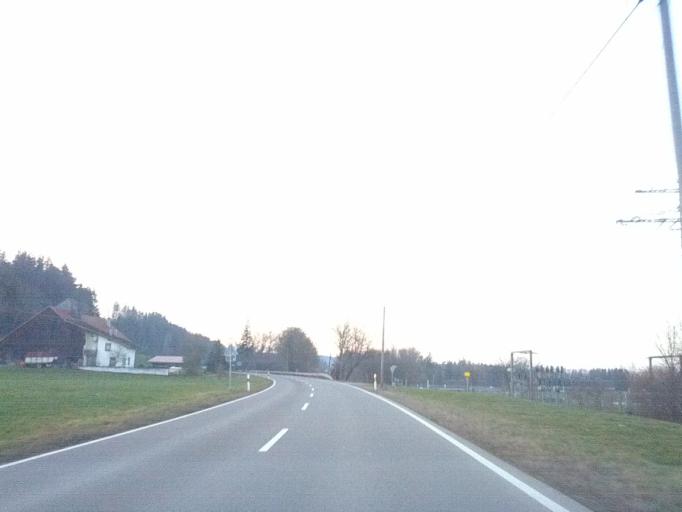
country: DE
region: Bavaria
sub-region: Swabia
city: Lautrach
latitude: 47.9169
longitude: 10.1122
